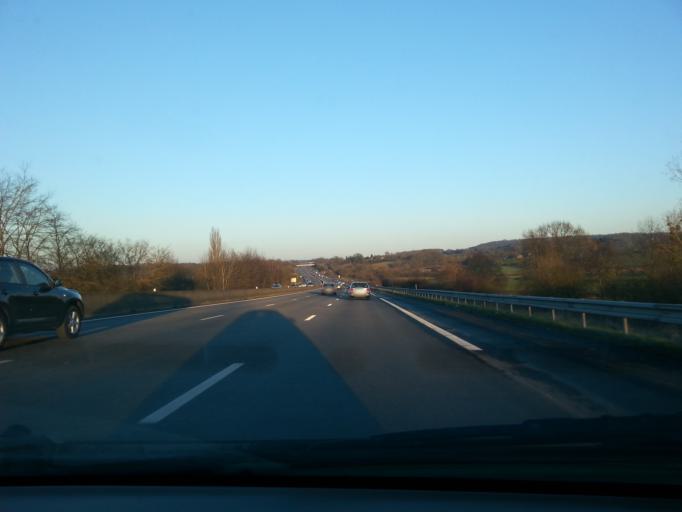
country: FR
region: Pays de la Loire
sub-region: Departement de la Sarthe
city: Cherre
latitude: 48.1562
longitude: 0.7137
